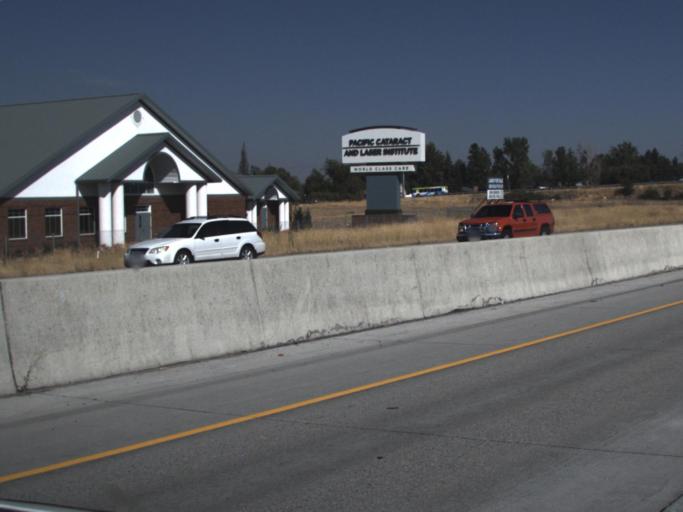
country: US
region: Washington
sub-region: Spokane County
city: Veradale
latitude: 47.6658
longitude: -117.1788
